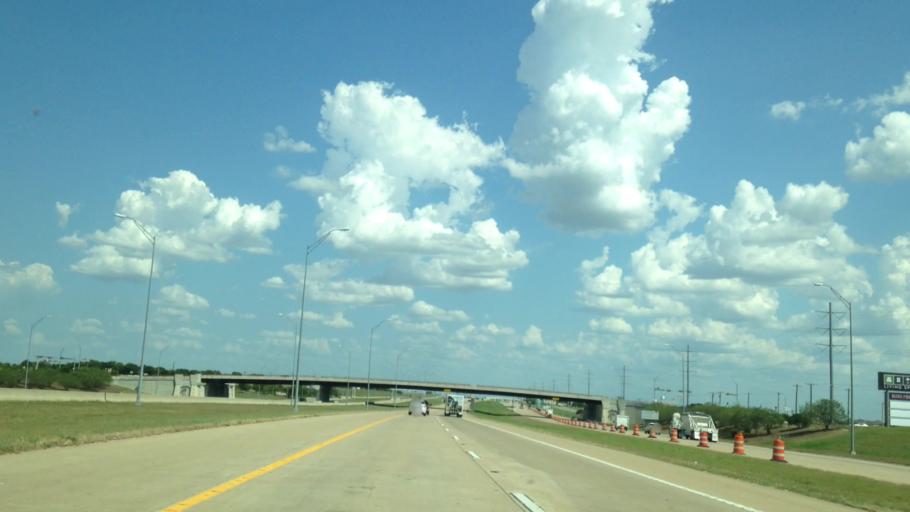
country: US
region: Texas
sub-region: Travis County
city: Windemere
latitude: 30.4849
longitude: -97.6168
